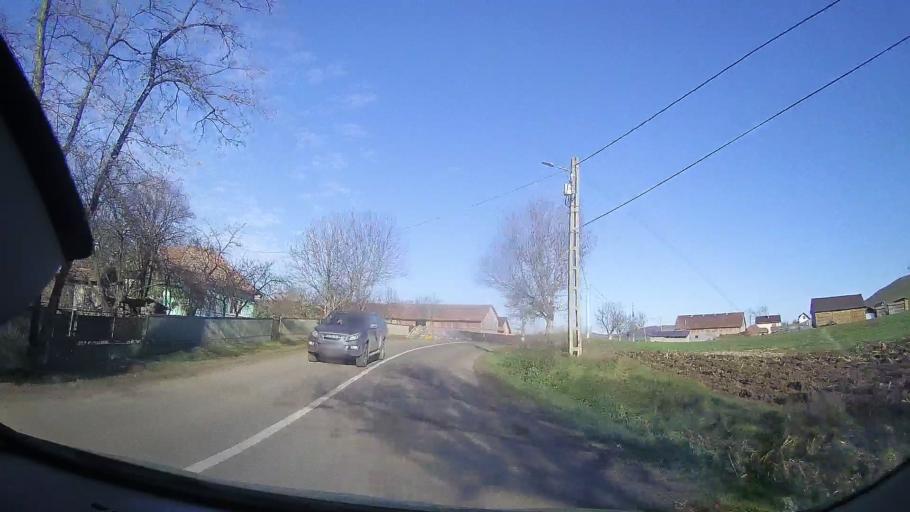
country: RO
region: Mures
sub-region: Comuna Band
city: Band
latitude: 46.5739
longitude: 24.3478
